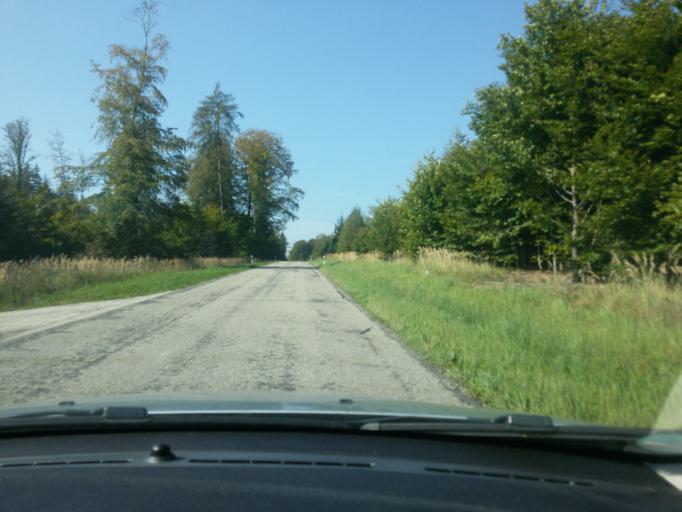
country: DE
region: Bavaria
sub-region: Swabia
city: Scherstetten
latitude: 48.1844
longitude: 10.6703
